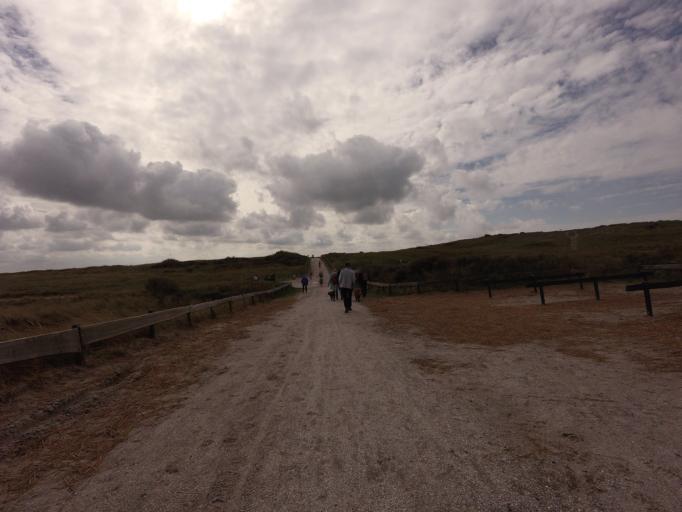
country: NL
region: Friesland
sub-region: Gemeente Ameland
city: Nes
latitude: 53.4620
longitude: 5.8347
